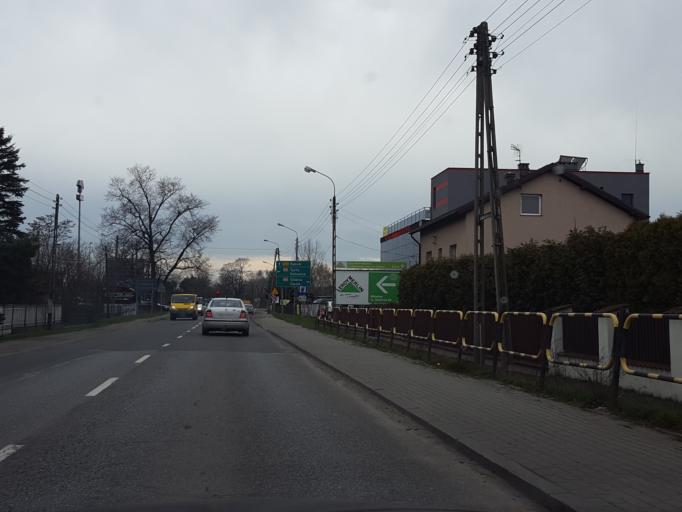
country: PL
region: Silesian Voivodeship
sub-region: Ruda Slaska
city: Ruda Slaska
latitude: 50.2222
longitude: 18.8284
